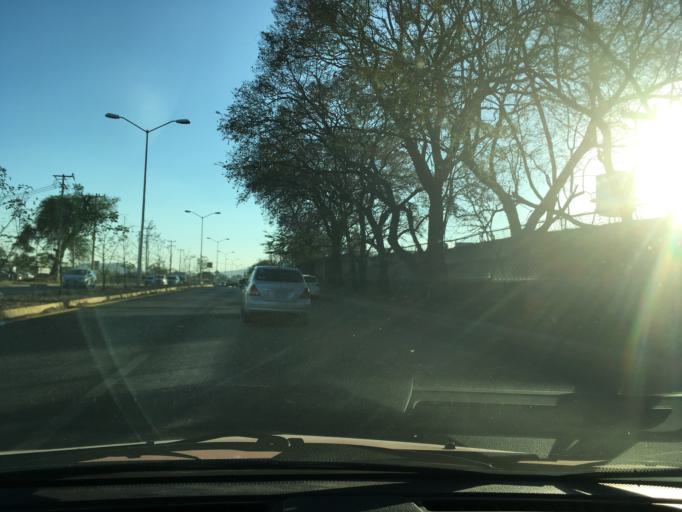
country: MX
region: Jalisco
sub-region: Tlajomulco de Zuniga
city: La Tijera
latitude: 20.5771
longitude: -103.4326
